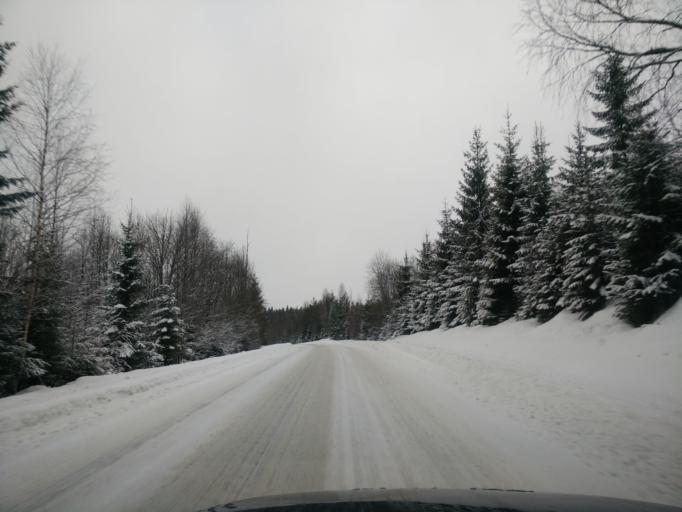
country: SE
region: Vaesternorrland
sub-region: Ange Kommun
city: Ange
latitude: 62.4768
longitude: 15.4724
